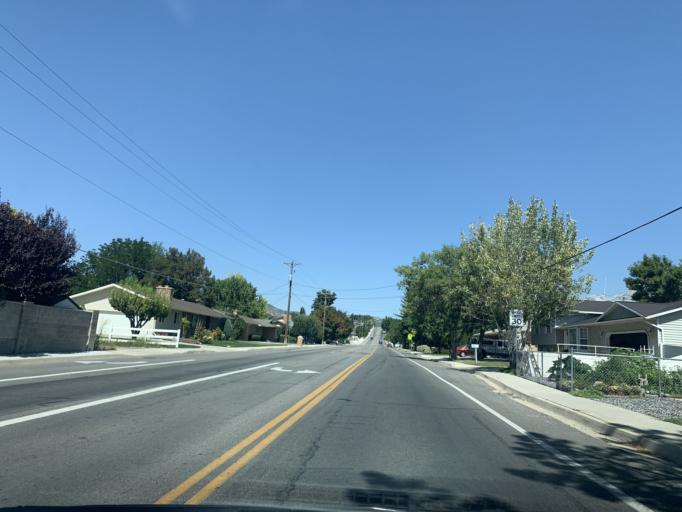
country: US
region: Utah
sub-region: Utah County
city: Lehi
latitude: 40.3991
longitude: -111.8302
